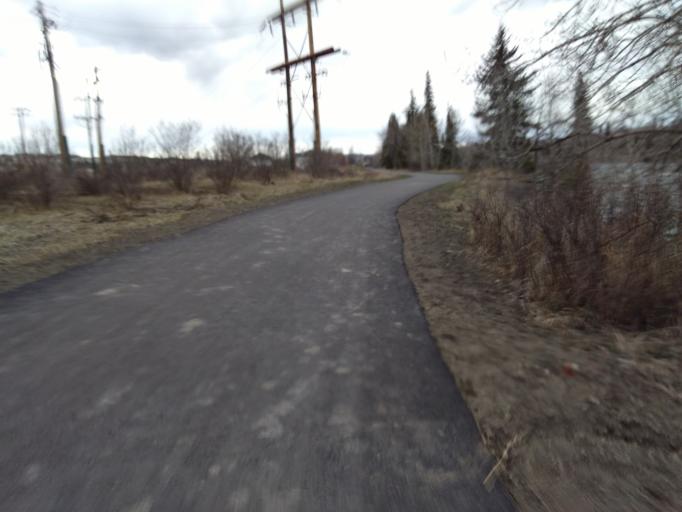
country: CA
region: Alberta
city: Cochrane
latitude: 51.1832
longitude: -114.4892
